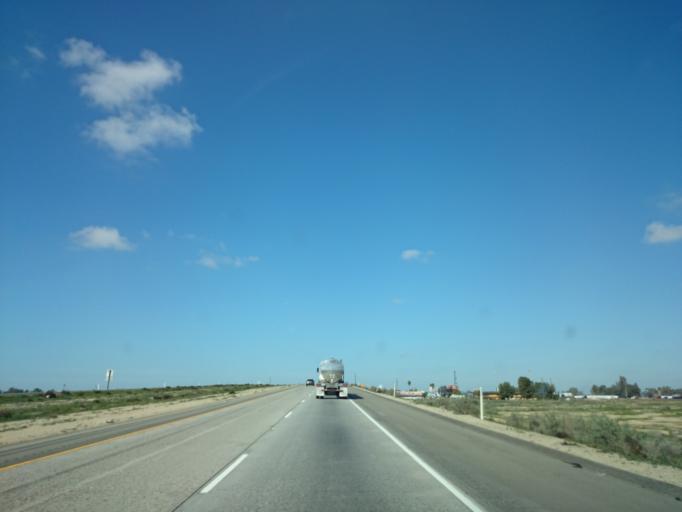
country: US
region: California
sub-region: Kern County
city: Buttonwillow
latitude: 35.3954
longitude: -119.3923
